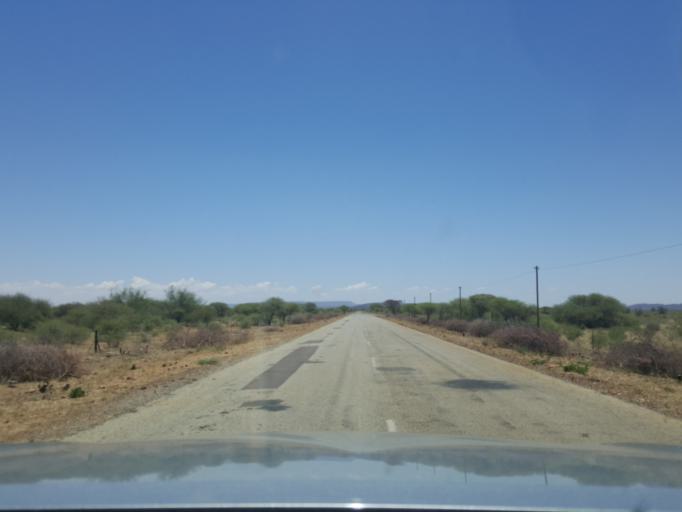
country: BW
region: South East
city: Ramotswa
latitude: -25.0334
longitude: 25.9266
